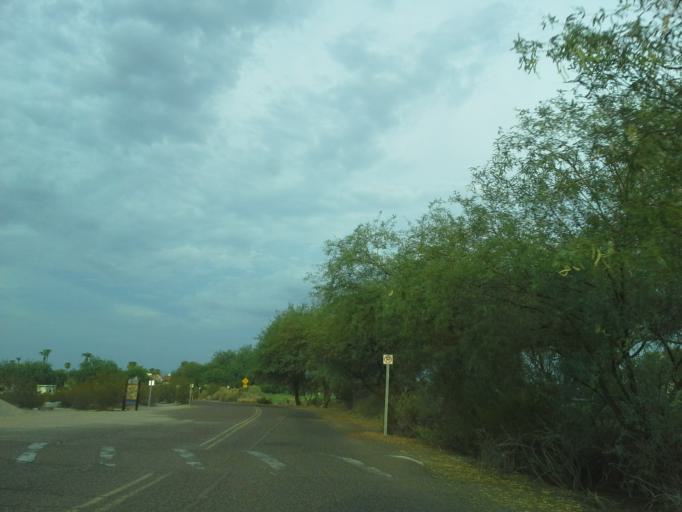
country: US
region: Arizona
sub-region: Maricopa County
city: Guadalupe
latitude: 33.3641
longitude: -111.9772
